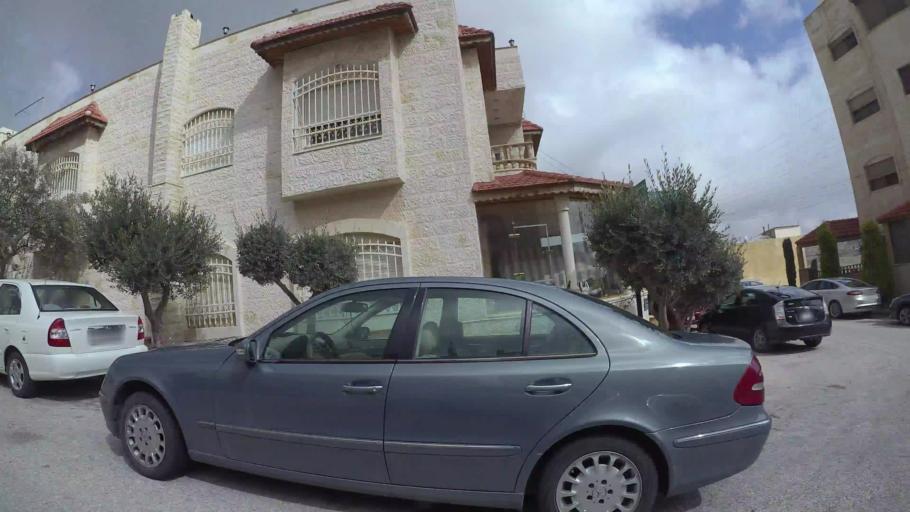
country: JO
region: Amman
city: Al Jubayhah
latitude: 32.0662
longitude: 35.8823
